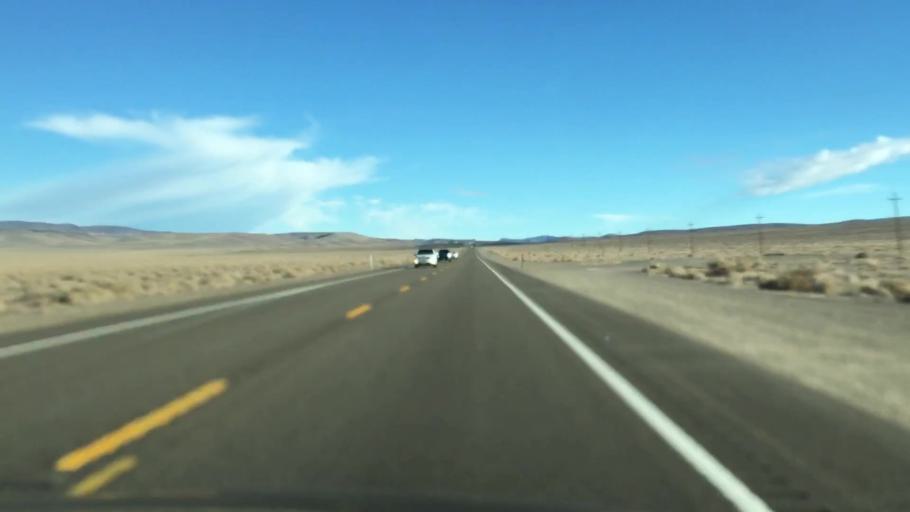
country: US
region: Nevada
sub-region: Mineral County
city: Hawthorne
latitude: 38.2538
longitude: -118.0806
